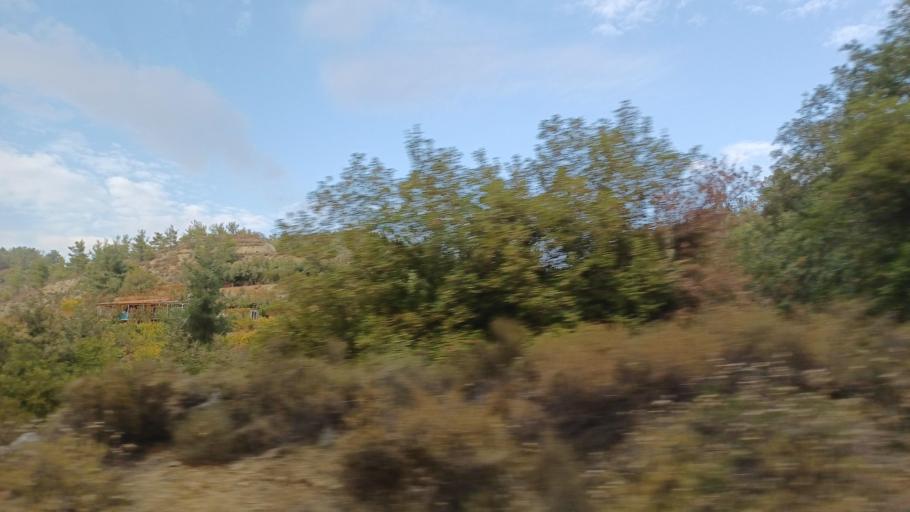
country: CY
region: Lefkosia
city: Kakopetria
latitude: 34.9745
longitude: 32.9128
